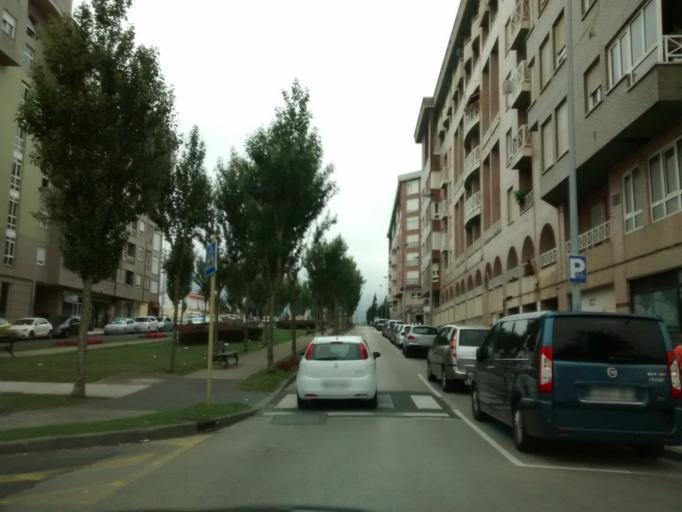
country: ES
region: Cantabria
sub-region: Provincia de Cantabria
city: Torrelavega
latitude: 43.3397
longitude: -4.0497
